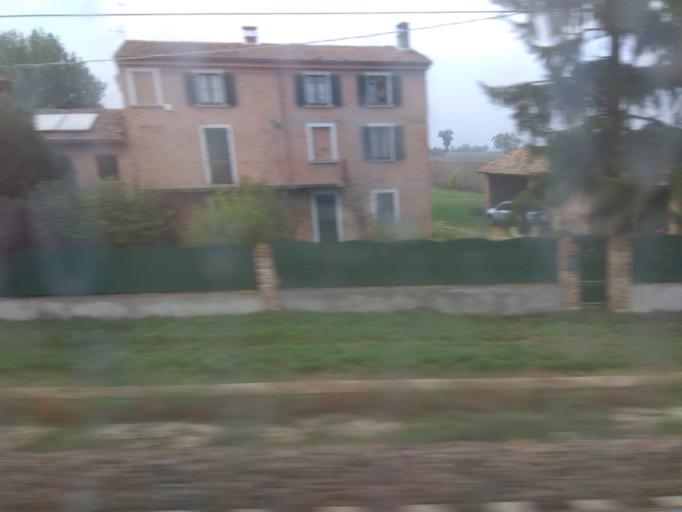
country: IT
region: Piedmont
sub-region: Provincia di Alessandria
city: Pontecurone
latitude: 44.9529
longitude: 8.9206
